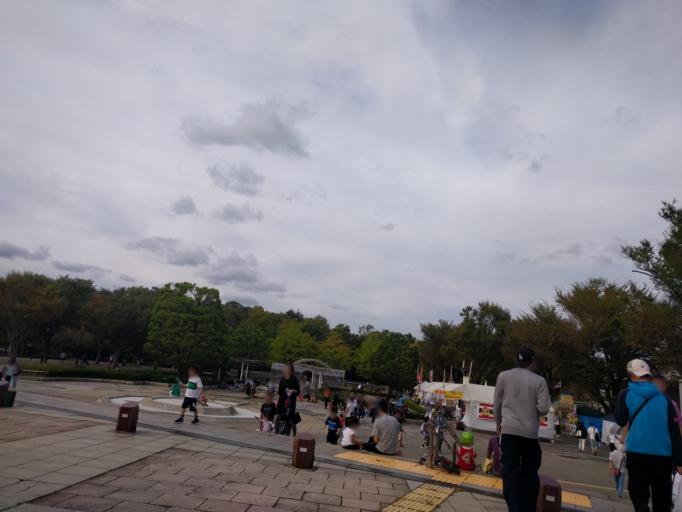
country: JP
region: Saitama
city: Wako
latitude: 35.7631
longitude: 139.6292
